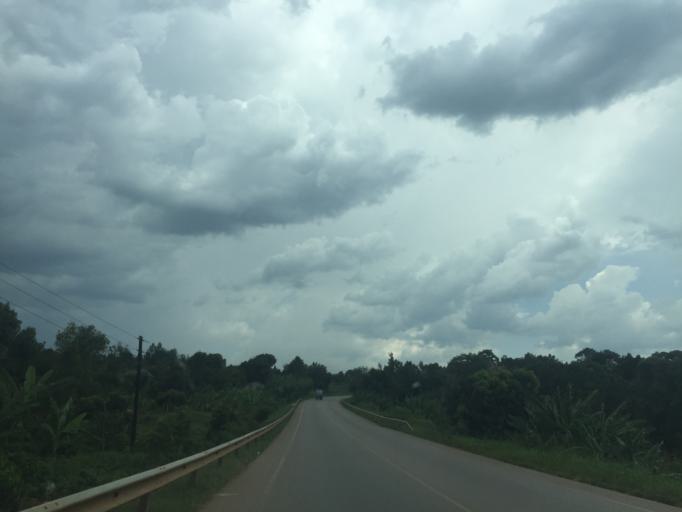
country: UG
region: Central Region
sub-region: Luwero District
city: Wobulenzi
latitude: 0.6752
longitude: 32.5275
